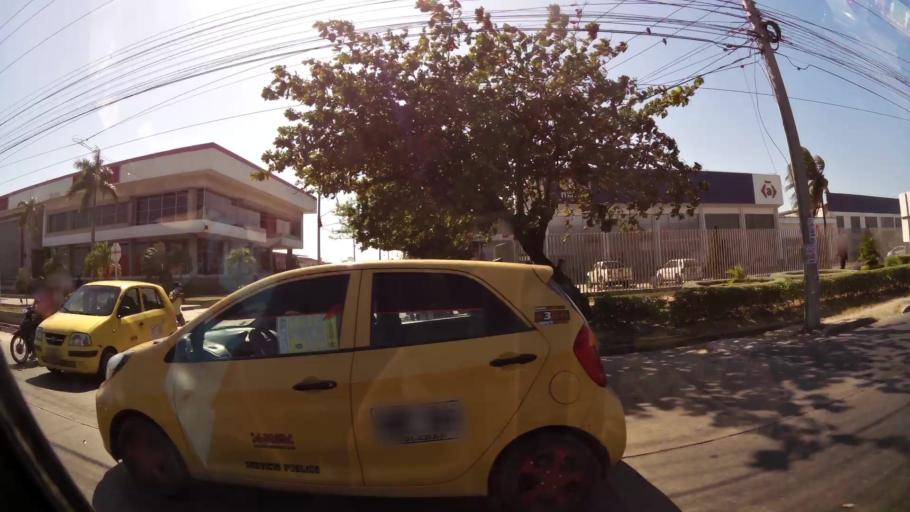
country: CO
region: Atlantico
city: Barranquilla
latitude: 10.9435
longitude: -74.7839
